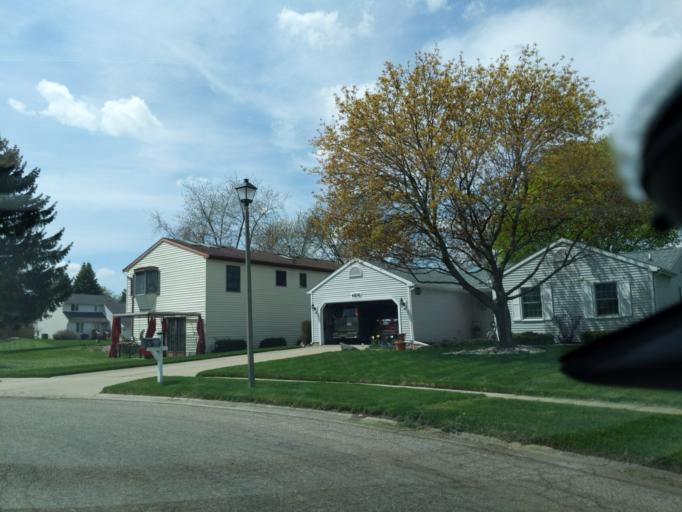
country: US
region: Michigan
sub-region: Eaton County
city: Waverly
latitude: 42.7278
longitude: -84.6184
